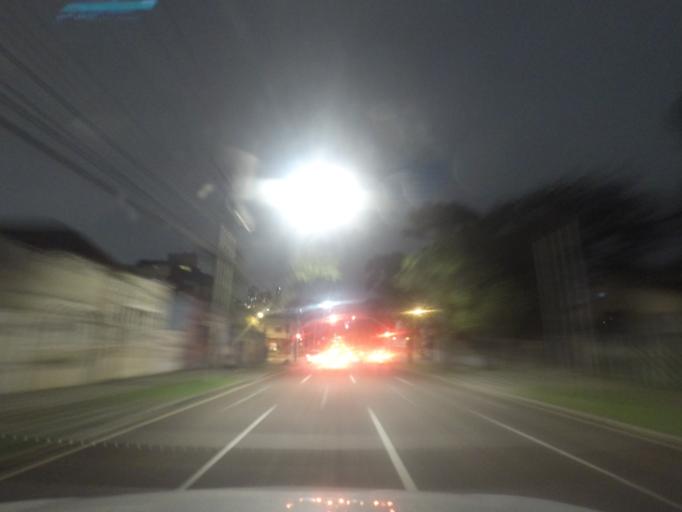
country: BR
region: Parana
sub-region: Curitiba
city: Curitiba
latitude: -25.4250
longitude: -49.2829
